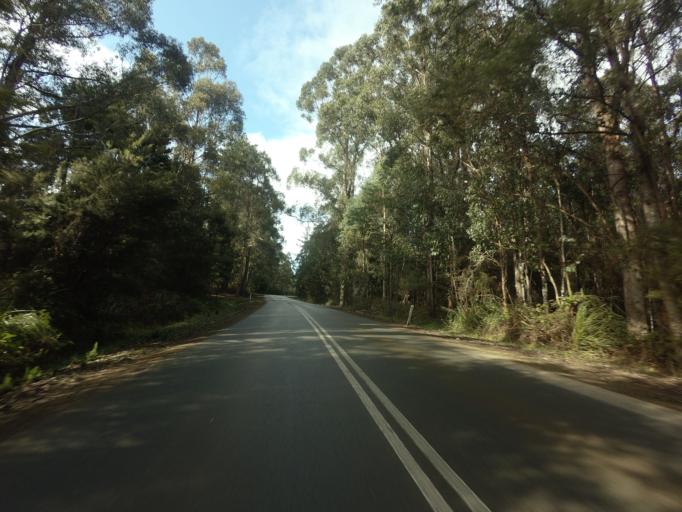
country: AU
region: Tasmania
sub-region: Huon Valley
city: Geeveston
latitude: -43.3526
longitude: 146.9568
